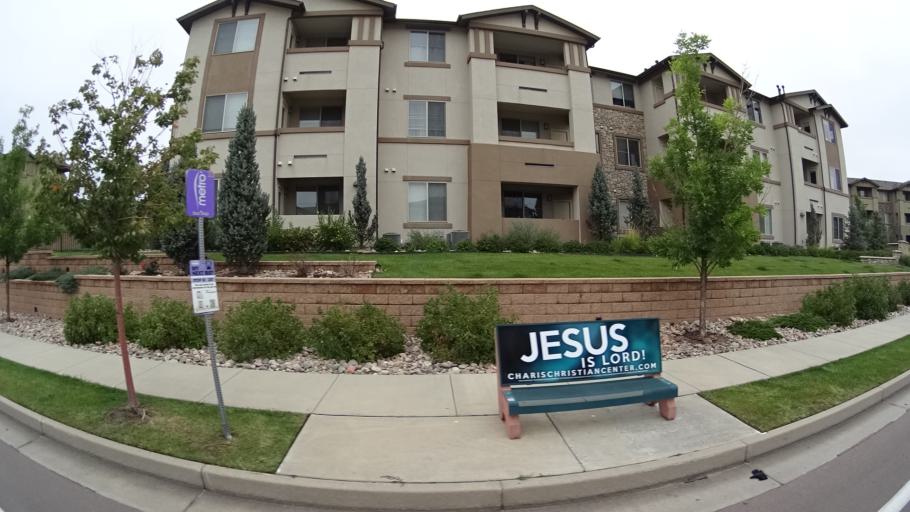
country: US
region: Colorado
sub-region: El Paso County
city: Cimarron Hills
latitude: 38.8842
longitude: -104.7135
